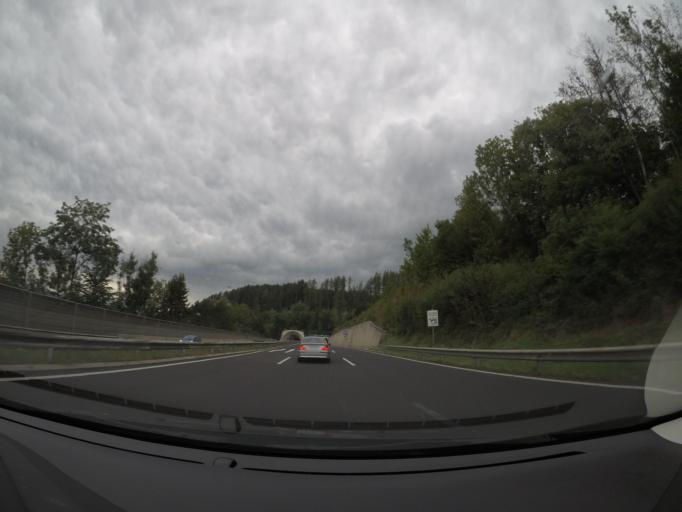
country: AT
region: Styria
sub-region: Politischer Bezirk Leoben
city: Leoben
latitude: 47.3688
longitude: 15.1058
